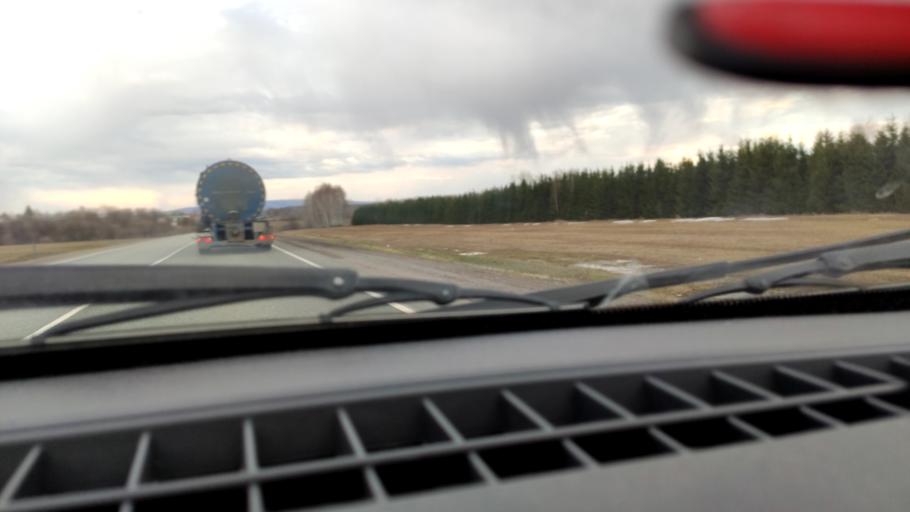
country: RU
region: Bashkortostan
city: Kudeyevskiy
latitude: 54.8166
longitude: 56.7199
